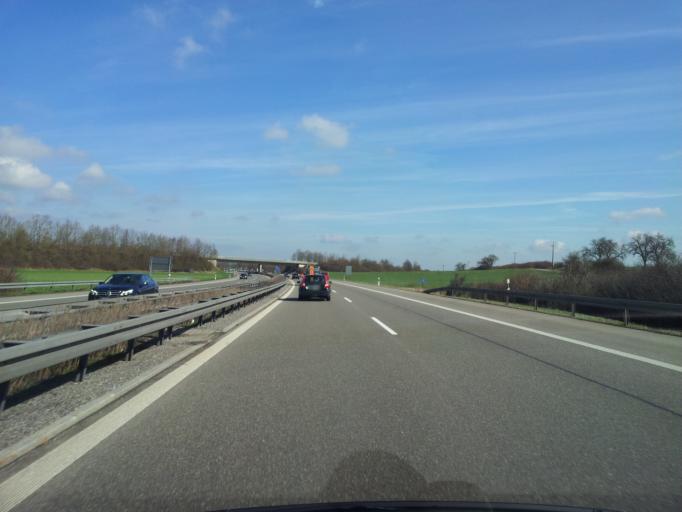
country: DE
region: Baden-Wuerttemberg
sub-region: Freiburg Region
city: Vohringen
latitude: 48.3171
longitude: 8.6462
